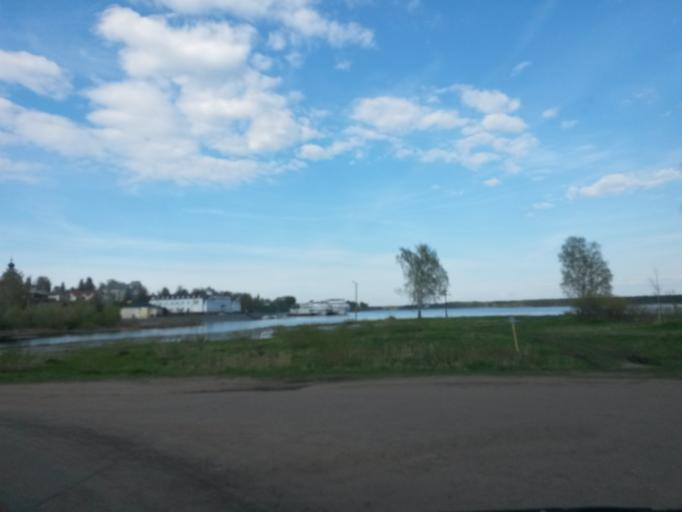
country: RU
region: Jaroslavl
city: Myshkin
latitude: 57.7829
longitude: 38.4533
